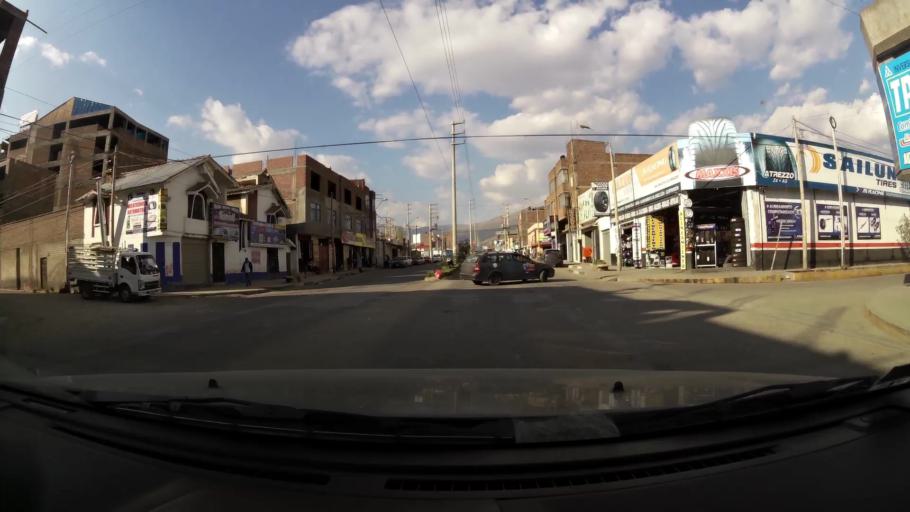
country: PE
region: Junin
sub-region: Provincia de Huancayo
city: El Tambo
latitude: -12.0560
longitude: -75.2214
